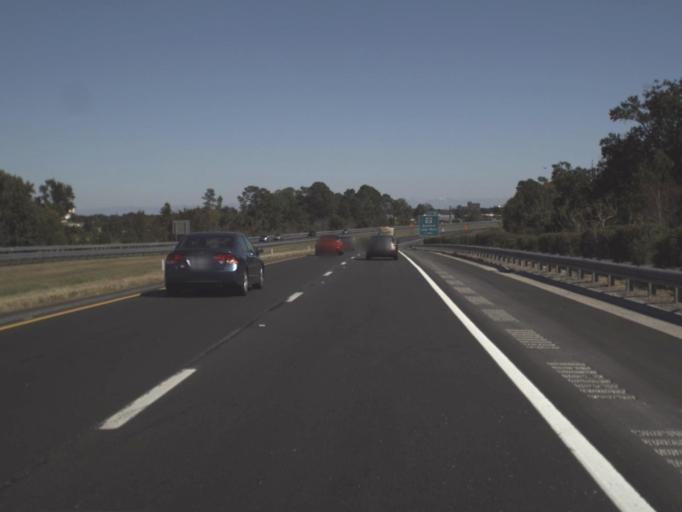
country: US
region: Florida
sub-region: Seminole County
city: Sanford
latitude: 28.7999
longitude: -81.3141
